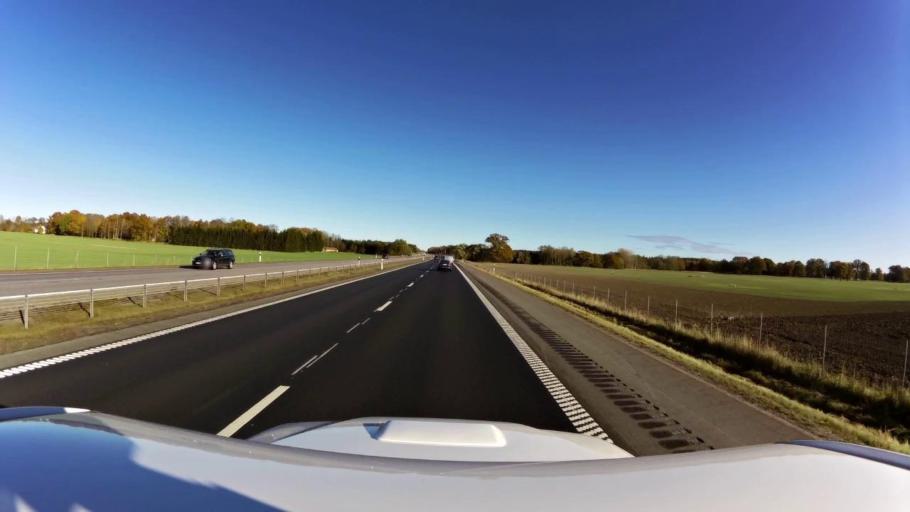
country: SE
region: OEstergoetland
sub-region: Linkopings Kommun
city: Vikingstad
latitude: 58.4113
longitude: 15.4638
